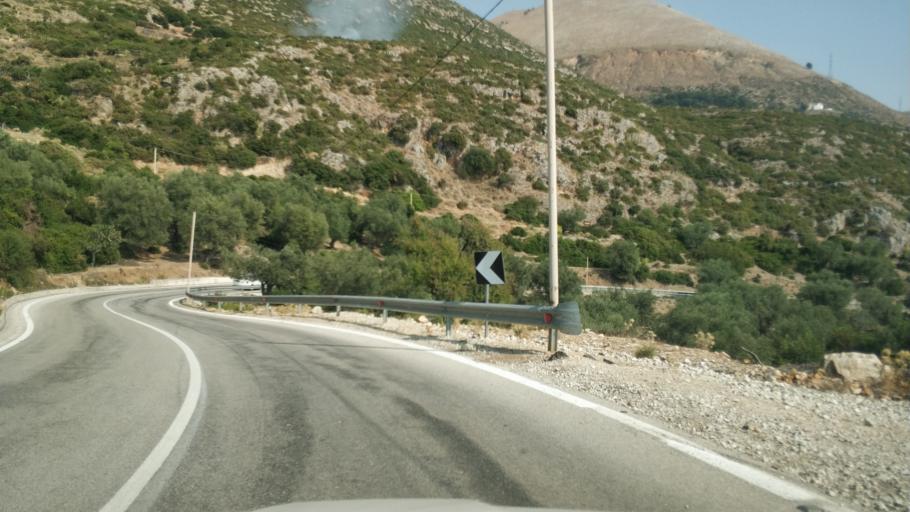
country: AL
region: Vlore
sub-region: Rrethi i Sarandes
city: Lukove
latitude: 40.0247
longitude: 19.8847
